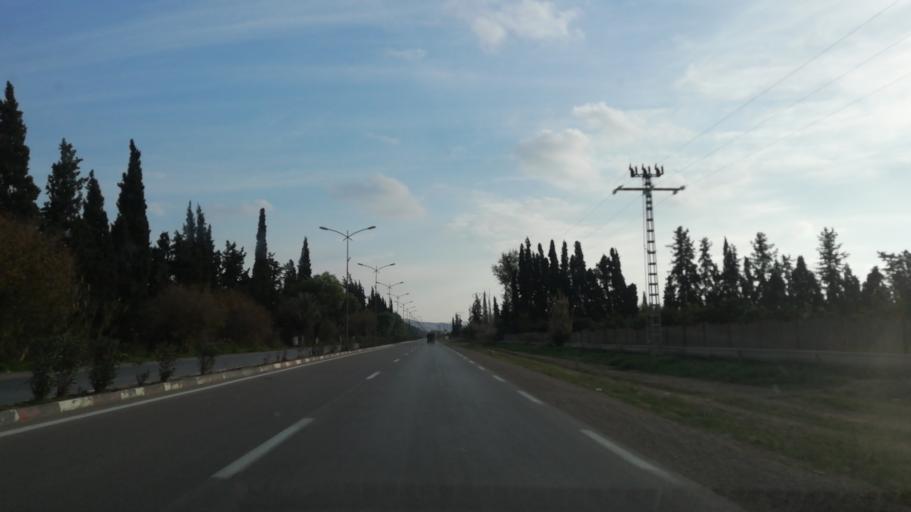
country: DZ
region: Mascara
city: Mascara
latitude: 35.6092
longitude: 0.0630
